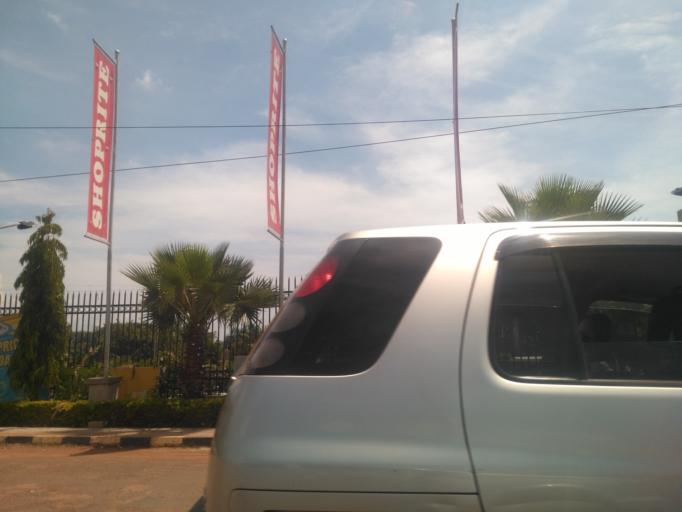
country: UG
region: Central Region
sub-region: Wakiso District
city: Entebbe
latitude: 0.0694
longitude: 32.4753
